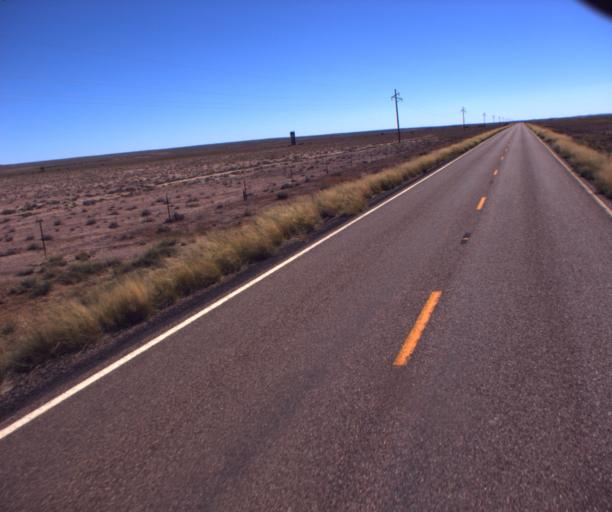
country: US
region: Arizona
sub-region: Navajo County
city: Holbrook
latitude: 35.1105
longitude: -110.0943
